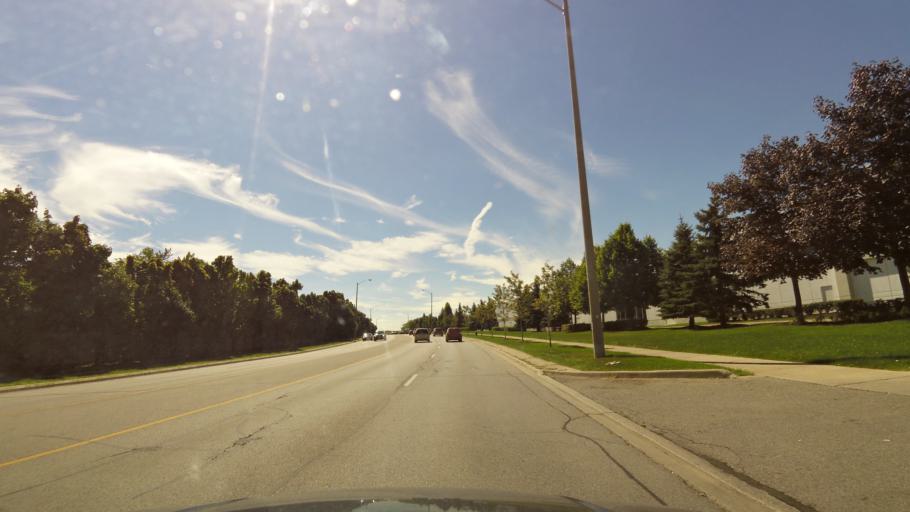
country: CA
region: Ontario
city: Mississauga
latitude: 43.6121
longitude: -79.6858
